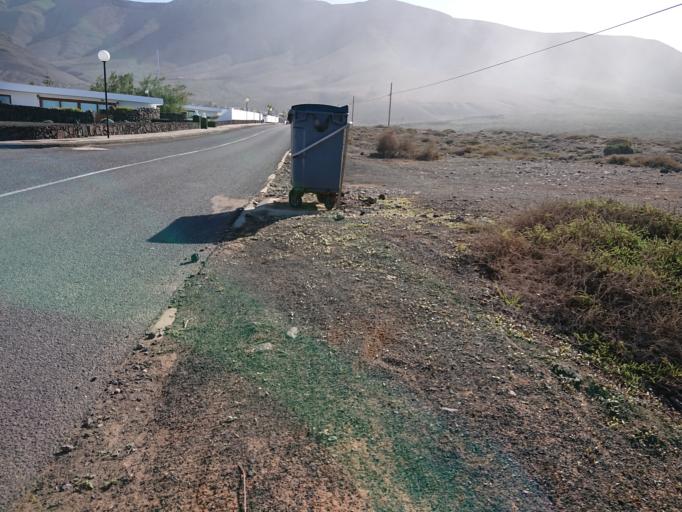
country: ES
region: Canary Islands
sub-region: Provincia de Las Palmas
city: Teguise
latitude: 29.1138
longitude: -13.5507
